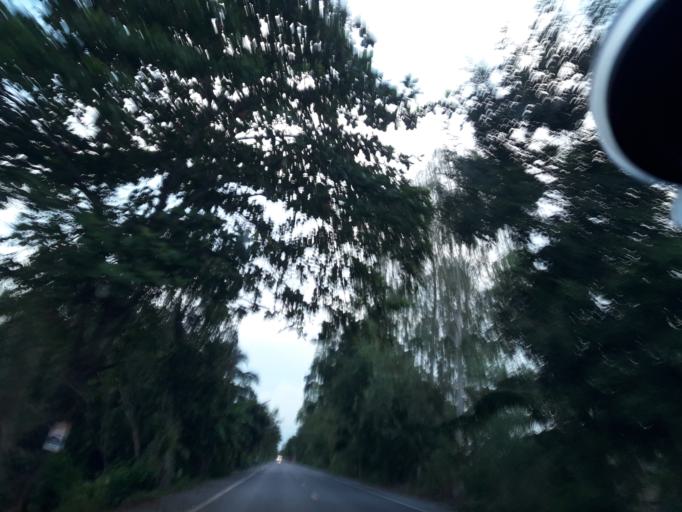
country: TH
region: Pathum Thani
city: Nong Suea
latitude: 14.1504
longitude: 100.8690
